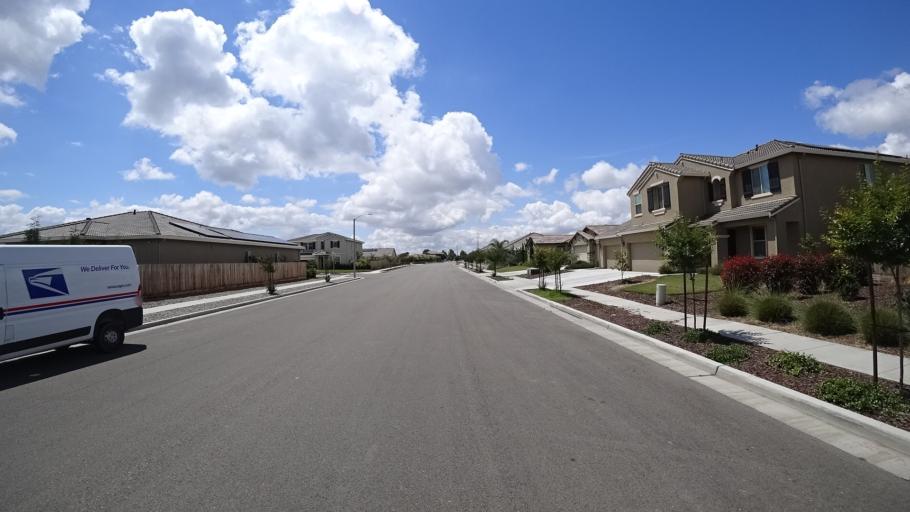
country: US
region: California
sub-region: Kings County
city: Lucerne
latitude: 36.3707
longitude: -119.6619
